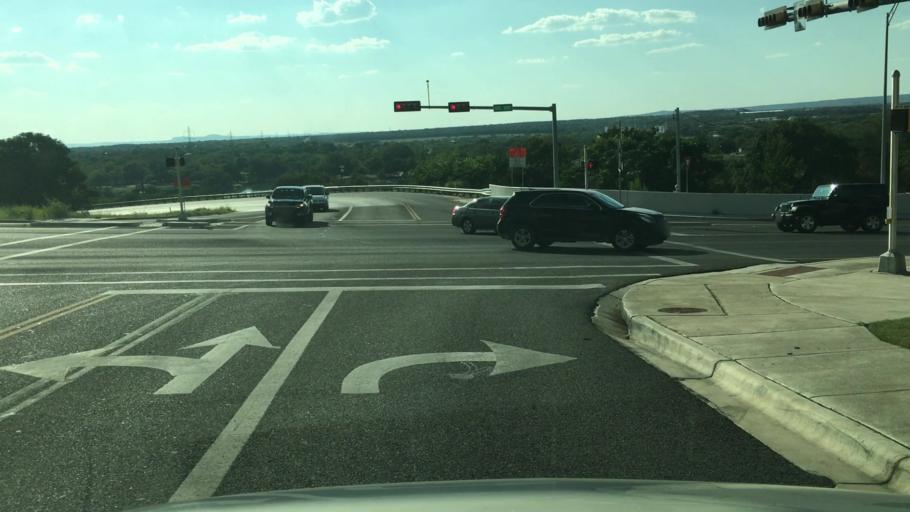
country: US
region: Texas
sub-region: Burnet County
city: Marble Falls
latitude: 30.5633
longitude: -98.2747
